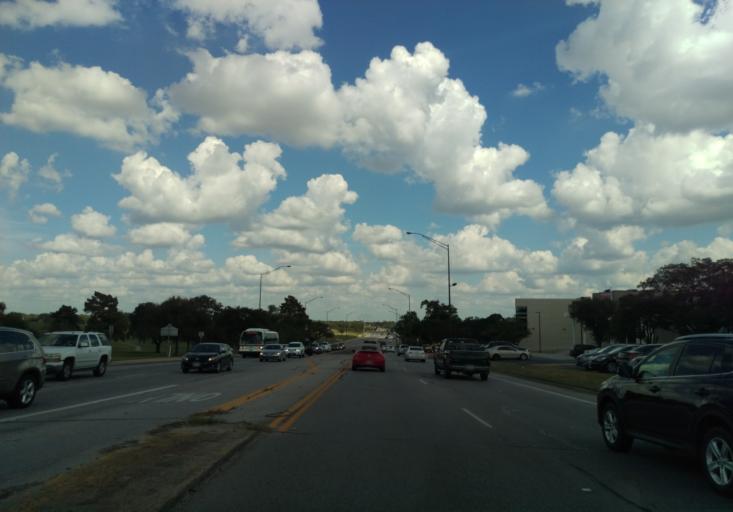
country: US
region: Texas
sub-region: Brazos County
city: College Station
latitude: 30.6120
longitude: -96.3311
